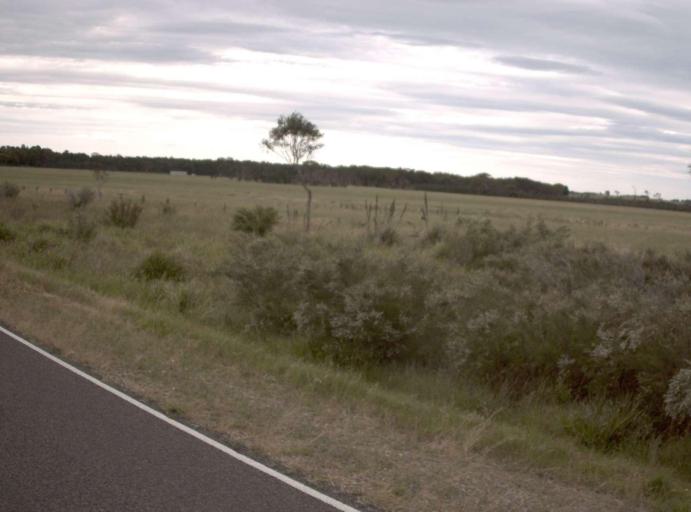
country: AU
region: Victoria
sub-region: East Gippsland
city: Bairnsdale
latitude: -37.9876
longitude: 147.3989
